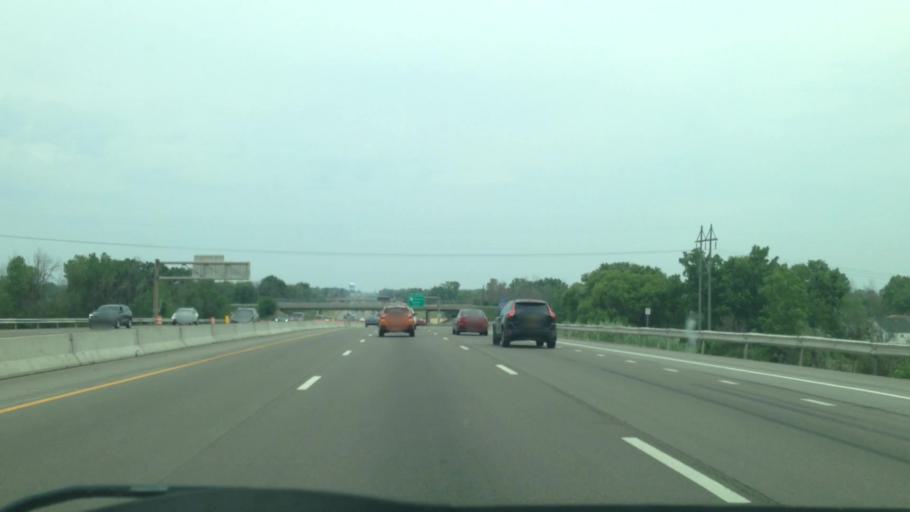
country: US
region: New York
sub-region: Erie County
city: Cheektowaga
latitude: 42.9156
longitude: -78.7663
